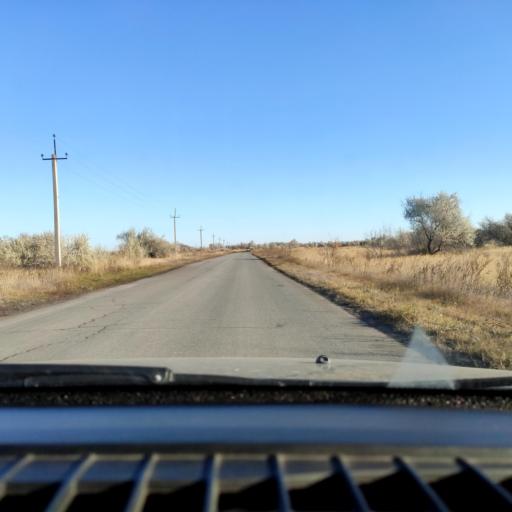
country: RU
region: Samara
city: Tol'yatti
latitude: 53.6534
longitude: 49.3265
